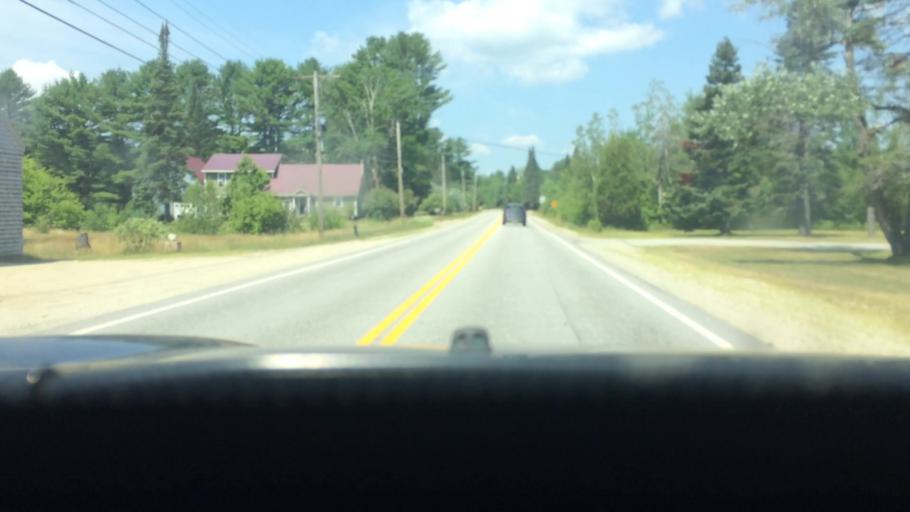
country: US
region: Maine
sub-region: Oxford County
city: Oxford
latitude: 44.1333
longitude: -70.4510
